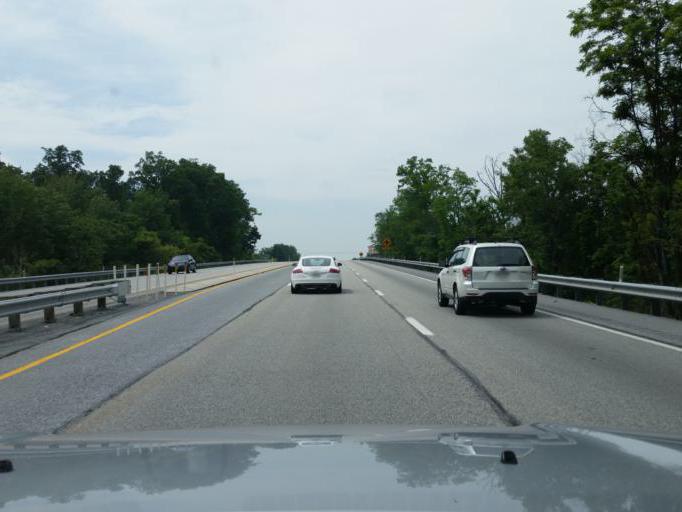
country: US
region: Pennsylvania
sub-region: York County
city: Dillsburg
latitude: 40.0915
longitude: -77.0469
